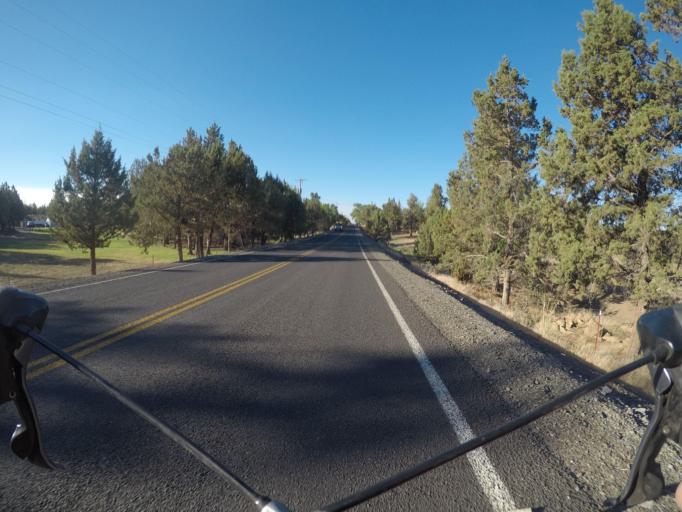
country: US
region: Oregon
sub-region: Deschutes County
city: Redmond
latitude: 44.2510
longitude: -121.2396
